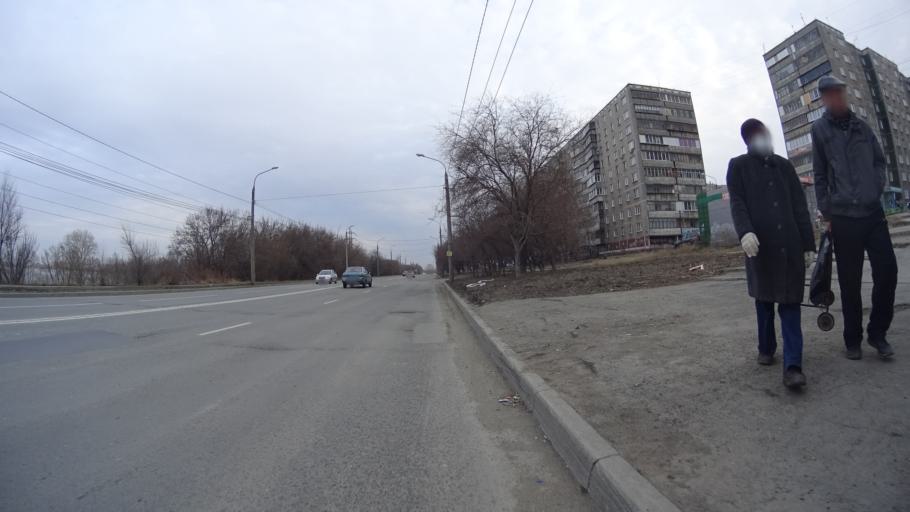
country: RU
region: Chelyabinsk
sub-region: Gorod Chelyabinsk
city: Chelyabinsk
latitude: 55.1841
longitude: 61.4853
